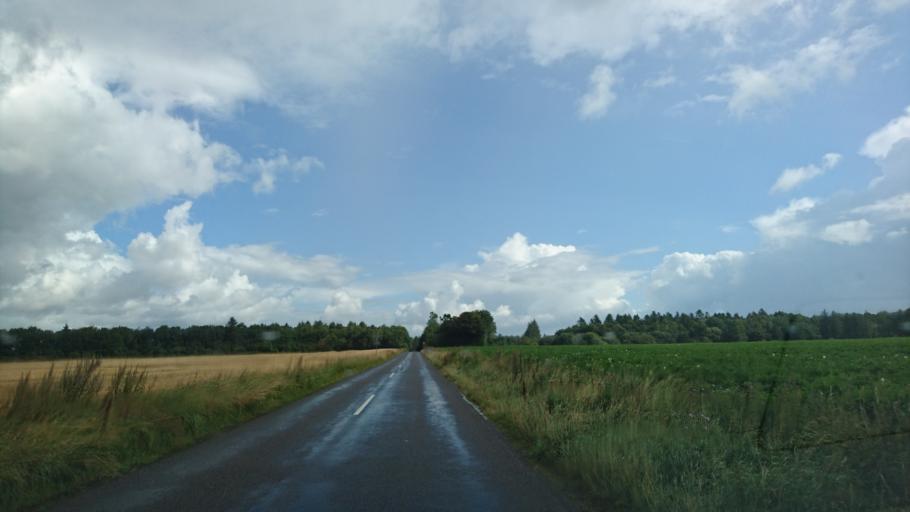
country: DK
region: North Denmark
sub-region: Hjorring Kommune
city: Sindal
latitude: 57.4690
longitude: 10.2550
